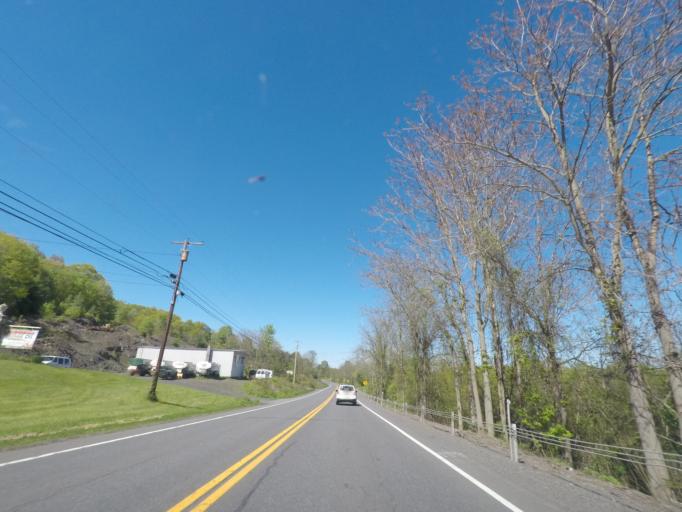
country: US
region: New York
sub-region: Greene County
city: Jefferson Heights
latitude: 42.2540
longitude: -73.8606
